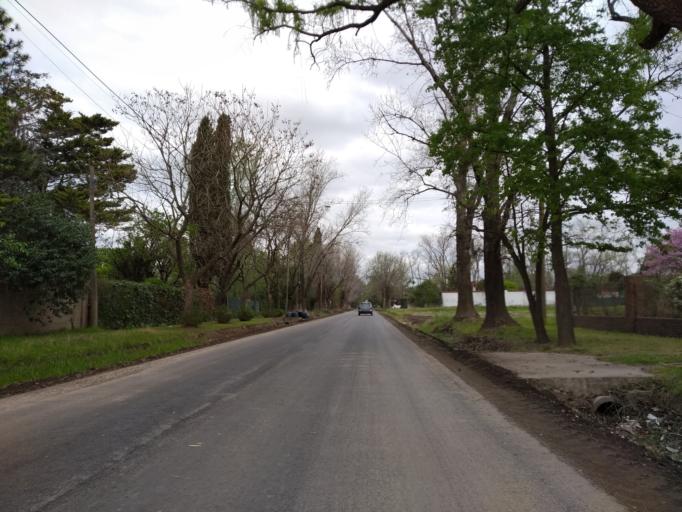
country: AR
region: Santa Fe
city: Funes
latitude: -32.9171
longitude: -60.8514
